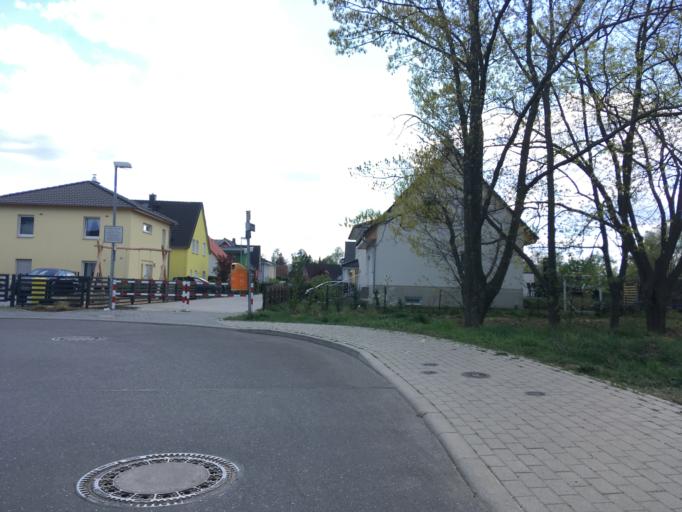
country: DE
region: Berlin
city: Mahlsdorf
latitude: 52.5174
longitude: 13.6366
